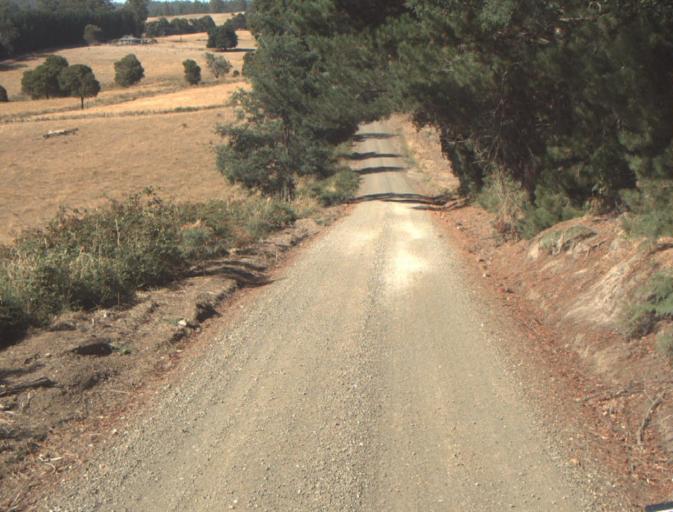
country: AU
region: Tasmania
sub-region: Launceston
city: Mayfield
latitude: -41.1677
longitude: 147.2118
